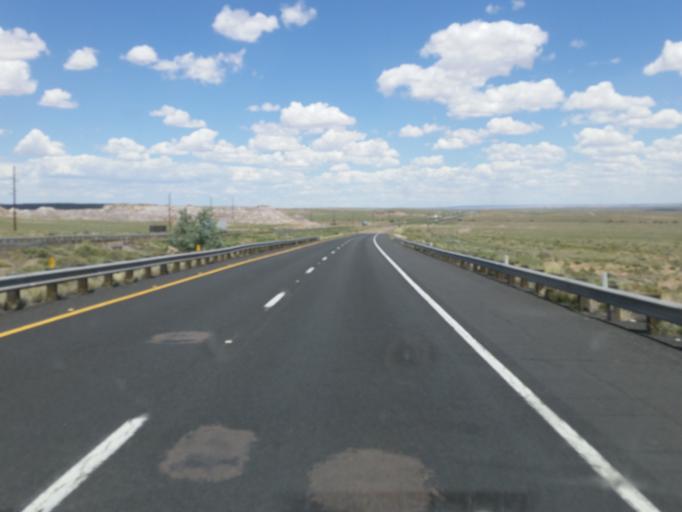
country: US
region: Arizona
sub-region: Navajo County
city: Holbrook
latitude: 34.9905
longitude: -109.9981
